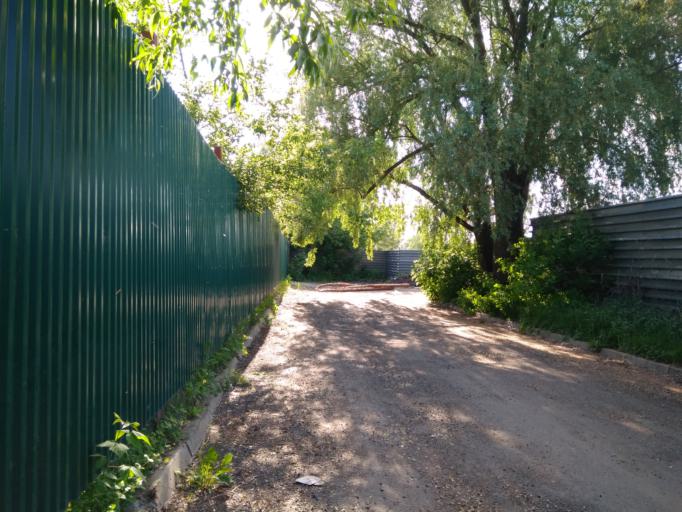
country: RU
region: Moskovskaya
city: Zhukovskiy
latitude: 55.5729
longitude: 38.0988
